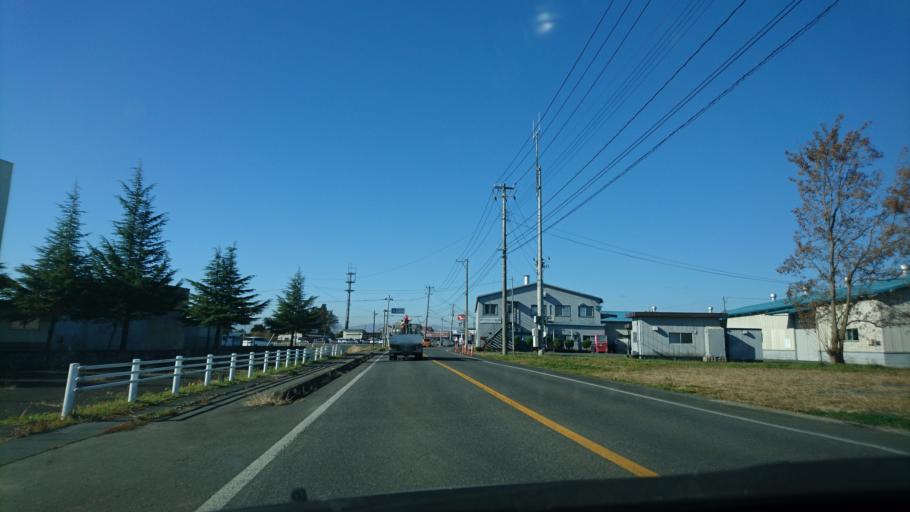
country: JP
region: Iwate
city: Mizusawa
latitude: 39.1432
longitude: 141.1101
